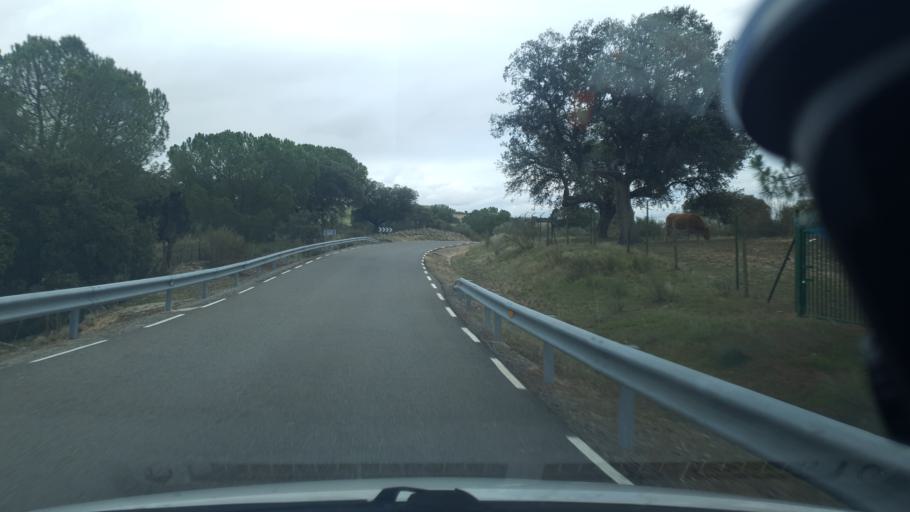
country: ES
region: Castille and Leon
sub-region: Provincia de Avila
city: Pozanco
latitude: 40.8265
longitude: -4.6926
